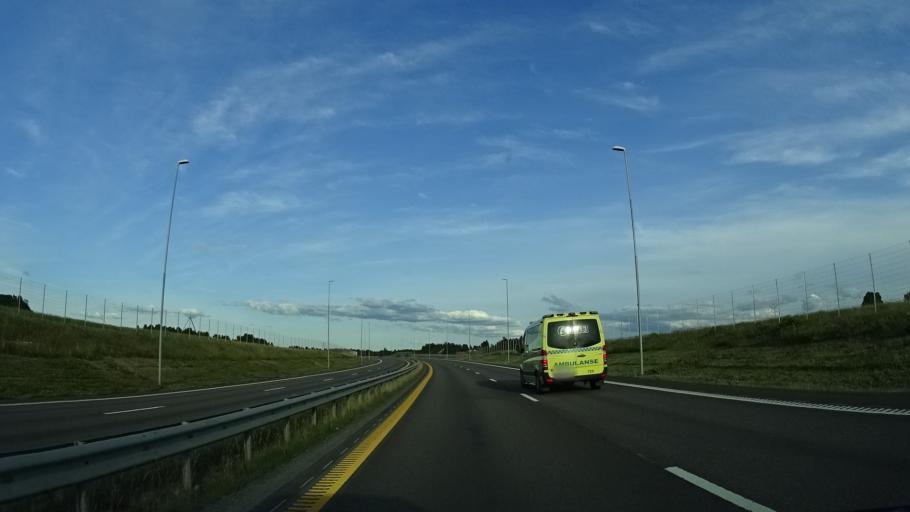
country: NO
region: Ostfold
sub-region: Hobol
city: Knappstad
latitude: 59.6071
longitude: 11.0353
